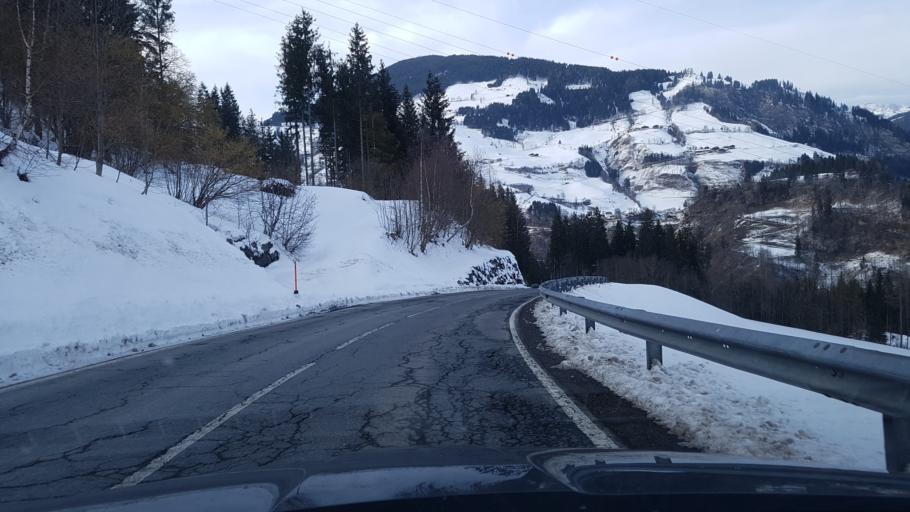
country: AT
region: Salzburg
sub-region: Politischer Bezirk Zell am See
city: Lend
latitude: 47.3003
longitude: 13.0274
